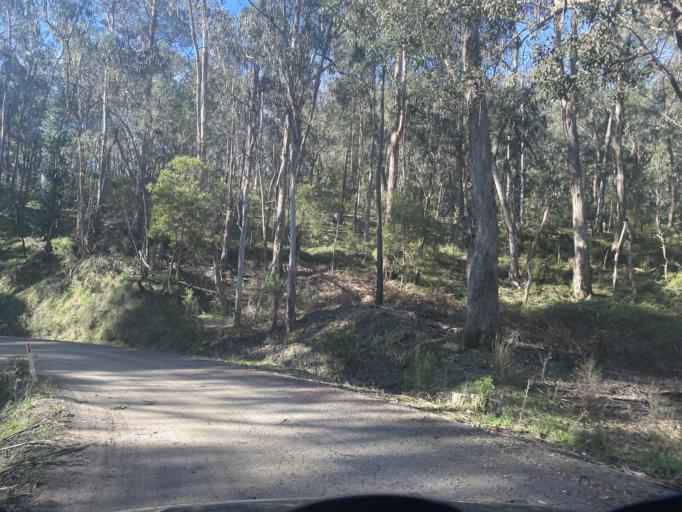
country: AU
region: Victoria
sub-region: Mansfield
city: Mansfield
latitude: -36.8244
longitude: 146.1535
